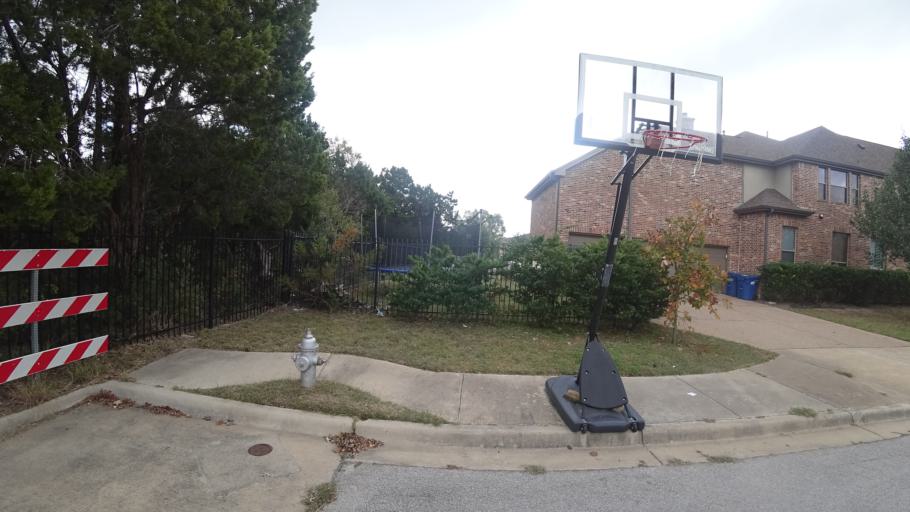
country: US
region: Texas
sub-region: Travis County
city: Barton Creek
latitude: 30.3175
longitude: -97.8996
